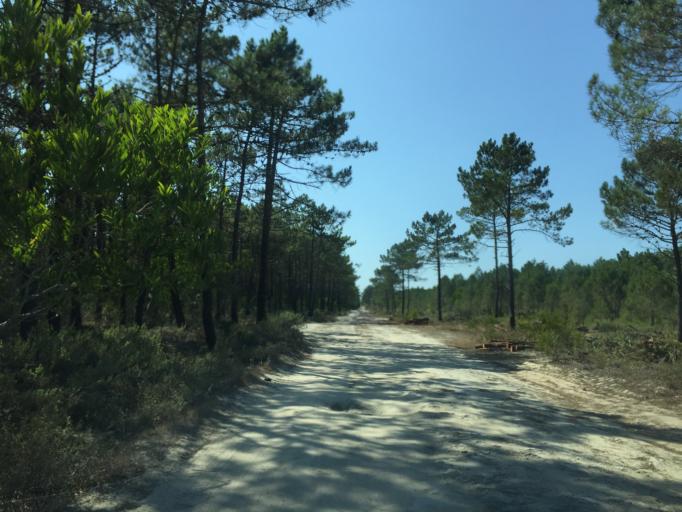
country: PT
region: Coimbra
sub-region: Figueira da Foz
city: Tavarede
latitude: 40.2589
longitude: -8.8445
